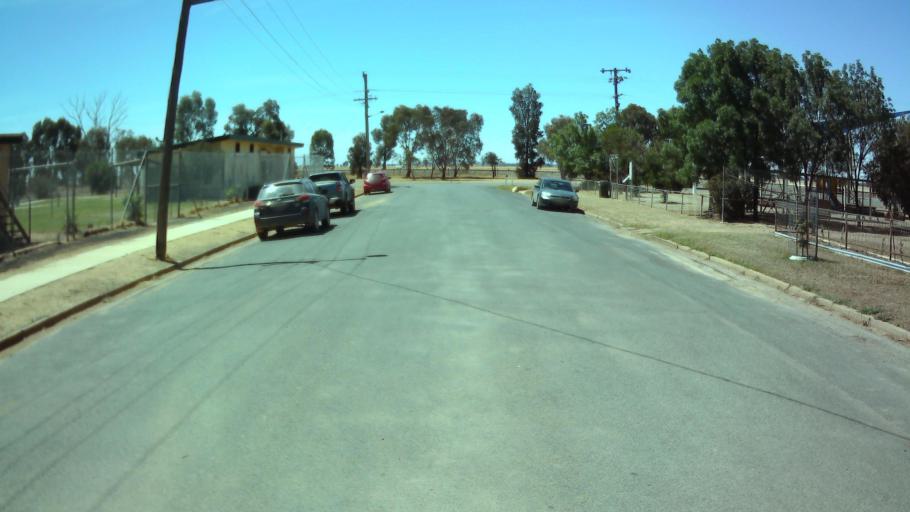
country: AU
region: New South Wales
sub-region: Weddin
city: Grenfell
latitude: -34.0104
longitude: 147.7933
